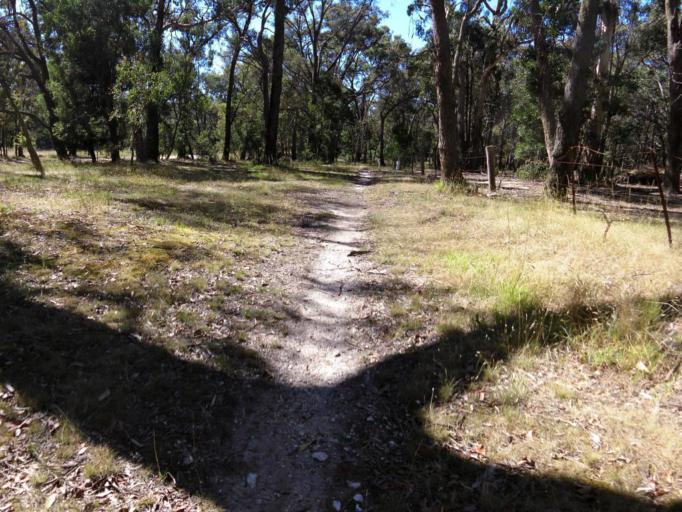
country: AU
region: Victoria
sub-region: Melton
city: Melton West
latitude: -37.5182
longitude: 144.5600
